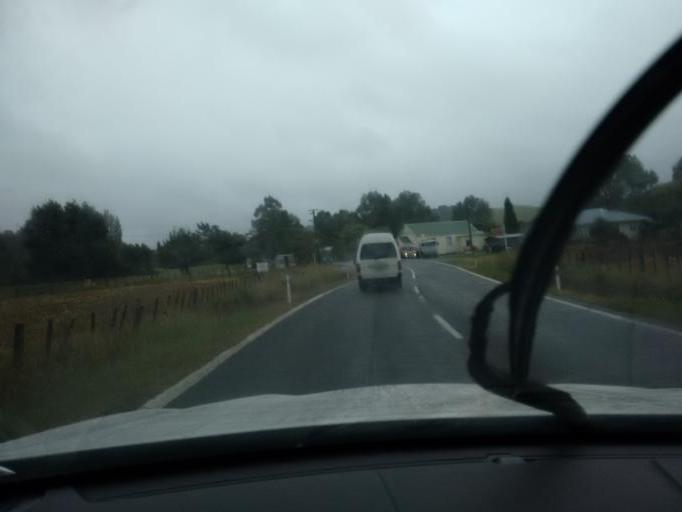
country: NZ
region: Waikato
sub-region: Thames-Coromandel District
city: Whitianga
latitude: -36.9230
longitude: 175.6982
